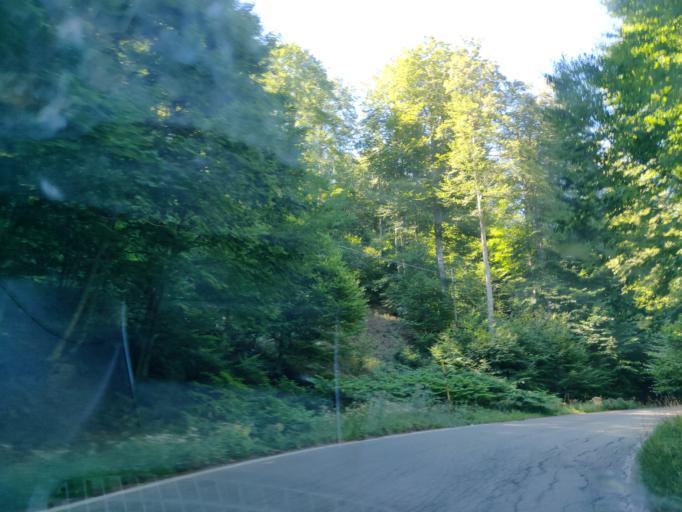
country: IT
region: Tuscany
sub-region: Provincia di Siena
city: Abbadia San Salvatore
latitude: 42.8988
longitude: 11.6155
